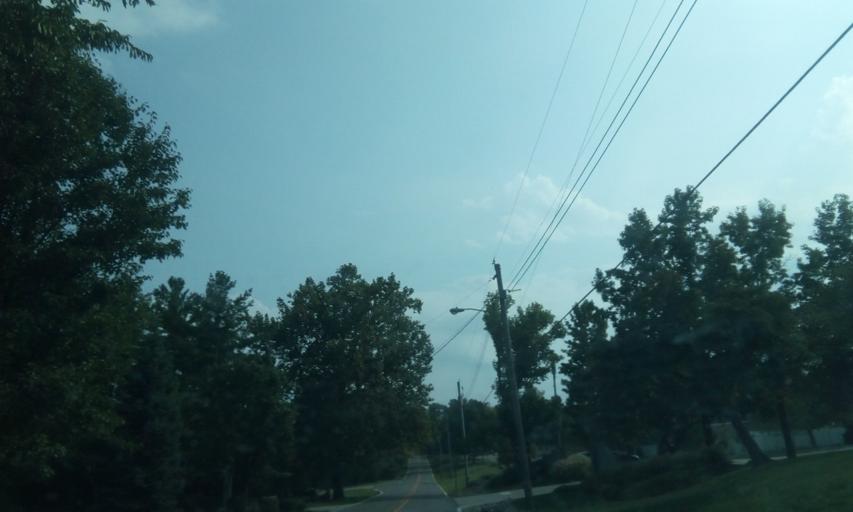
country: US
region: Missouri
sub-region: Saint Louis County
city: Town and Country
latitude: 38.6114
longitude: -90.4850
